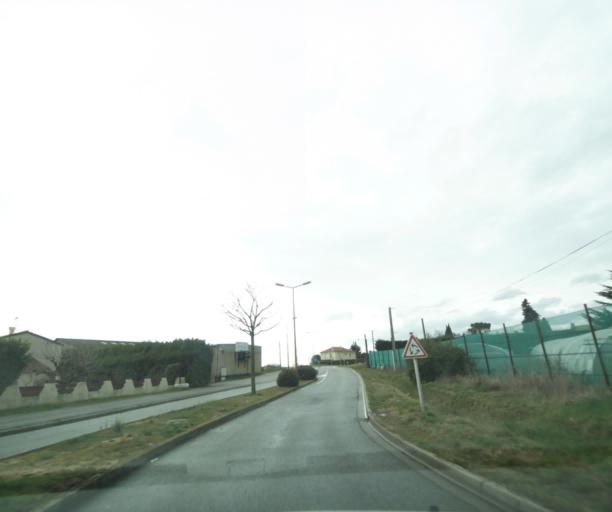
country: FR
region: Rhone-Alpes
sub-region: Departement de la Drome
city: Bourg-les-Valence
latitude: 44.9572
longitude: 4.9145
